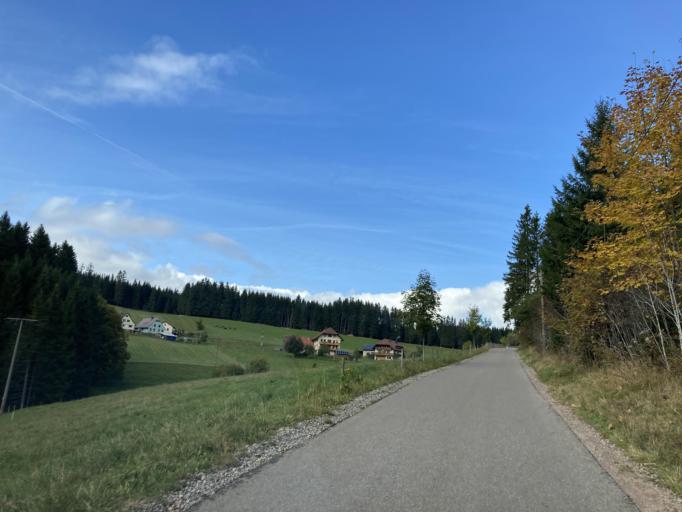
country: DE
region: Baden-Wuerttemberg
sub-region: Freiburg Region
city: Vohrenbach
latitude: 48.0703
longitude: 8.2822
